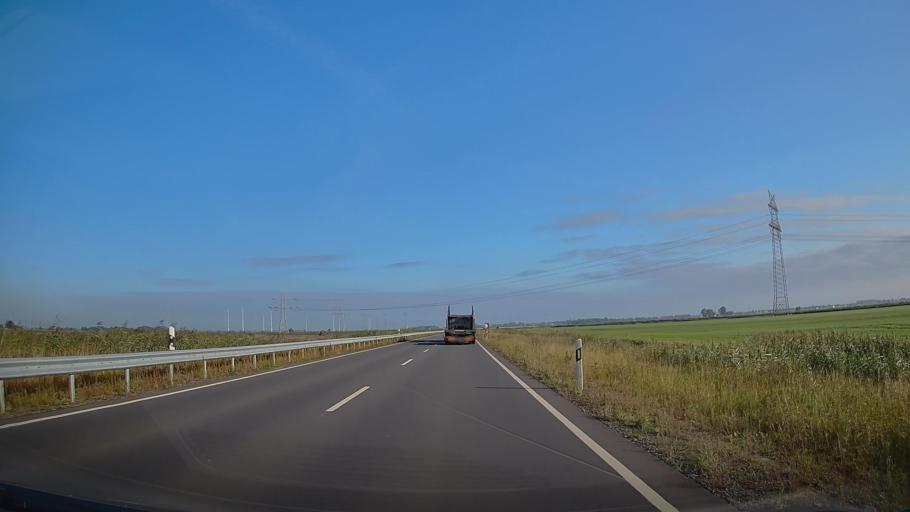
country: DE
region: Lower Saxony
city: Ovelgonne
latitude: 53.3144
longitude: 8.4002
